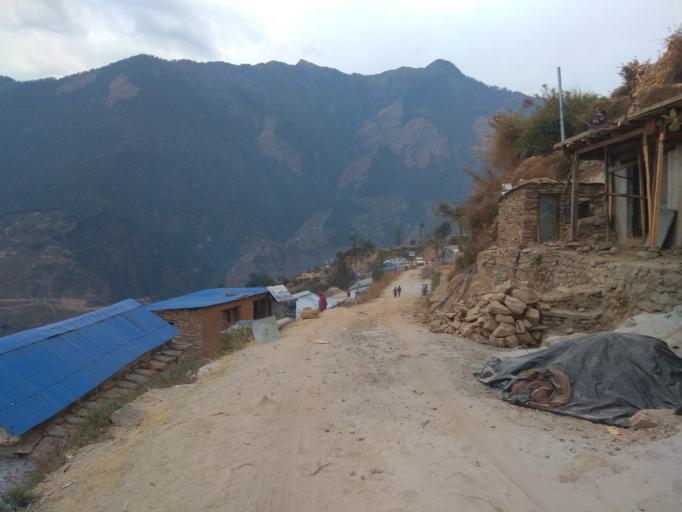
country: NP
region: Far Western
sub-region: Seti Zone
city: Achham
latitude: 29.2589
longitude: 81.6216
